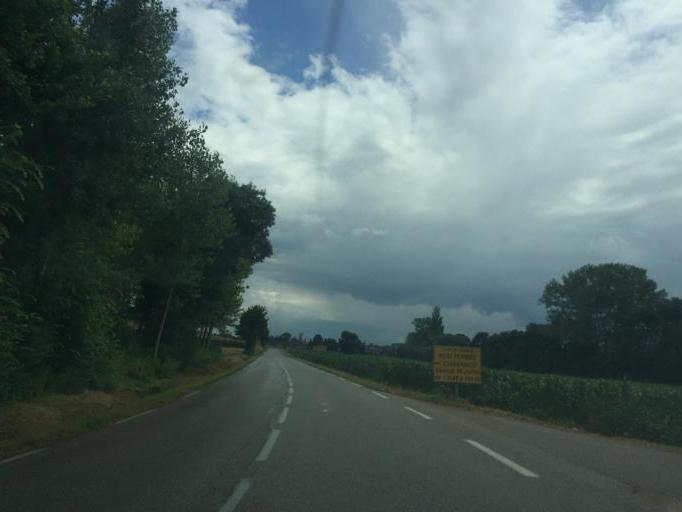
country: FR
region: Rhone-Alpes
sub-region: Departement du Rhone
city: Jons
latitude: 45.7982
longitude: 5.0989
